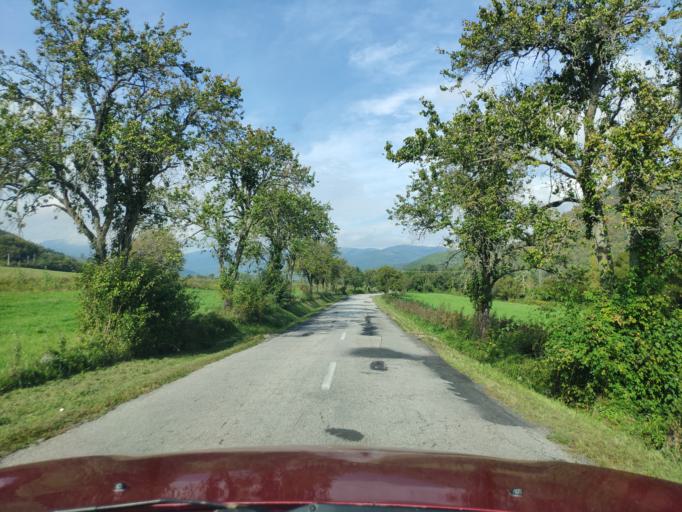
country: SK
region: Kosicky
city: Dobsina
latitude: 48.6900
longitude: 20.3199
